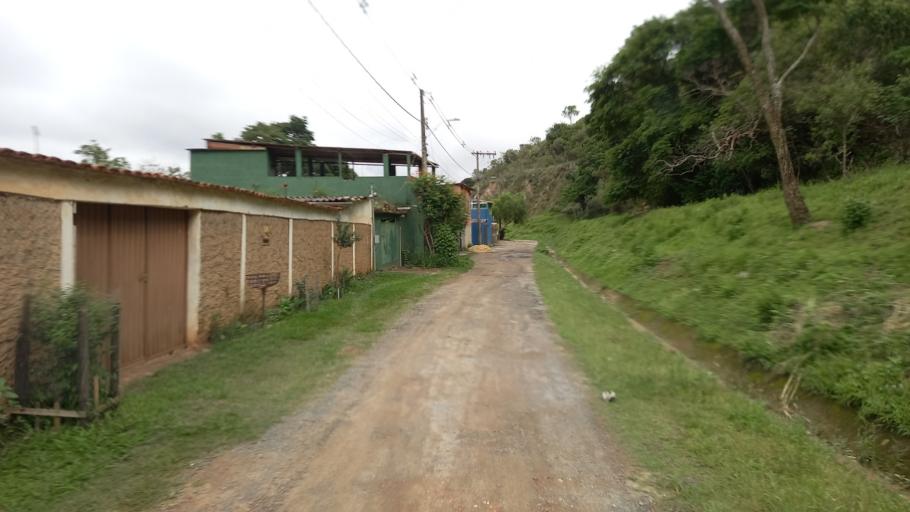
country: BR
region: Minas Gerais
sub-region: Belo Horizonte
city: Belo Horizonte
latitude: -19.9238
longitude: -43.8841
